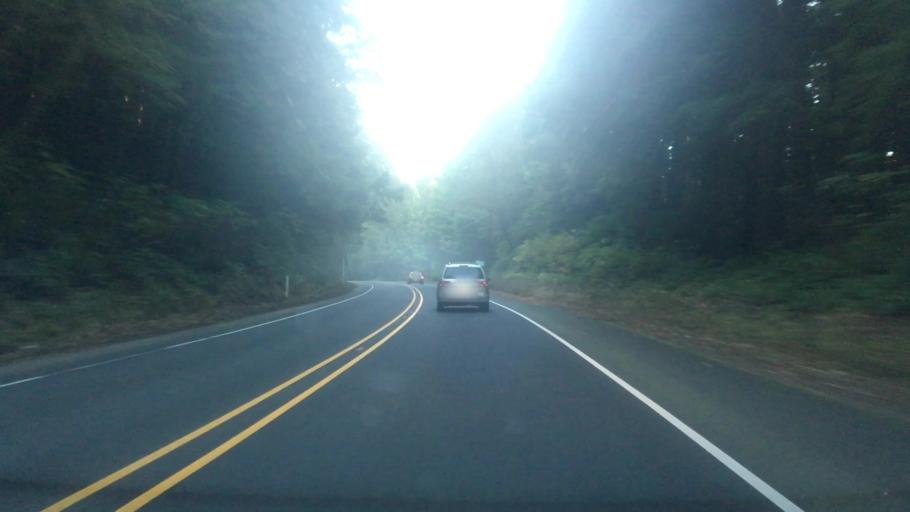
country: US
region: Oregon
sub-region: Clatsop County
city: Cannon Beach
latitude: 45.7828
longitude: -123.9572
